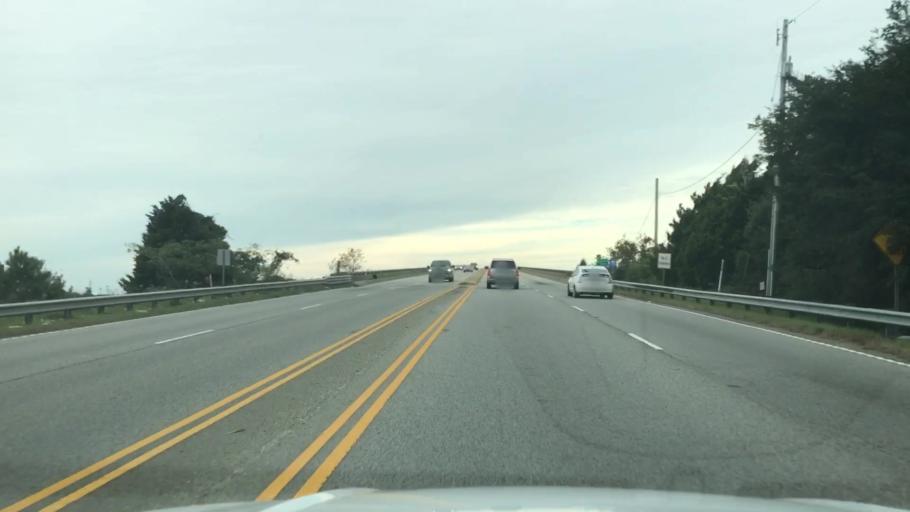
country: US
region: South Carolina
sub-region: Georgetown County
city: Georgetown
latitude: 33.3652
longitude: -79.2482
